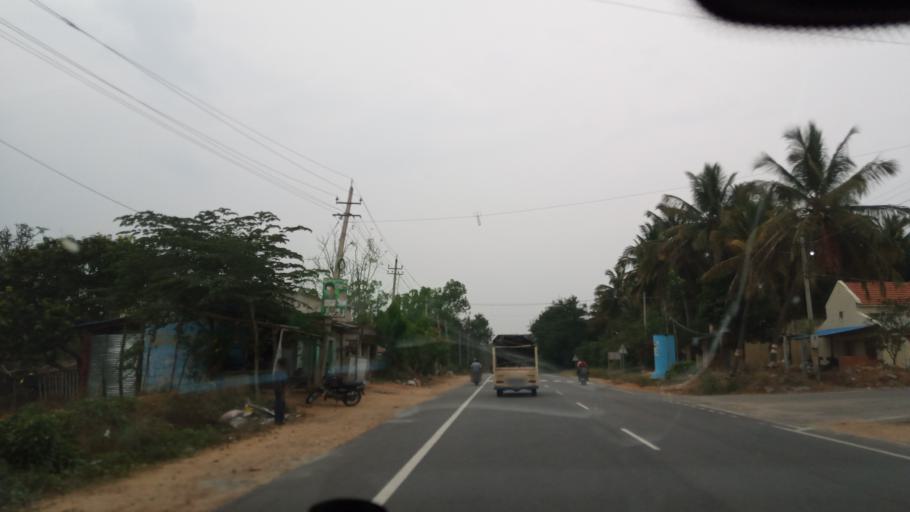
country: IN
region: Karnataka
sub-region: Mandya
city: Belluru
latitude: 12.9297
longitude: 76.7495
